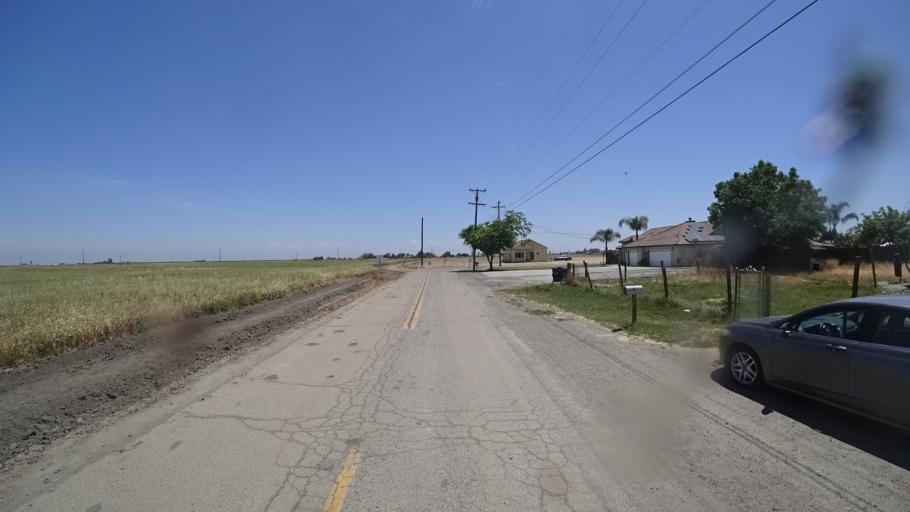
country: US
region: California
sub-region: Kings County
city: Corcoran
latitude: 36.1198
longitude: -119.5777
